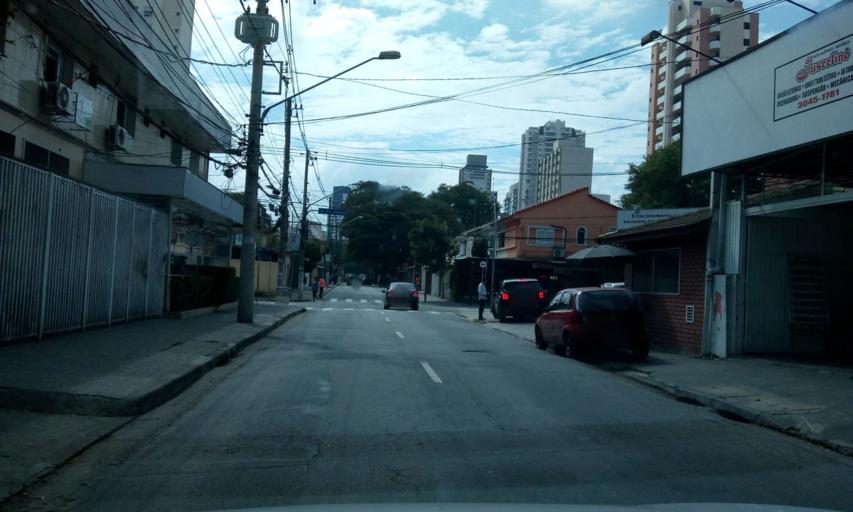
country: BR
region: Sao Paulo
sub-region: Sao Paulo
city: Sao Paulo
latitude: -23.6023
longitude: -46.6800
